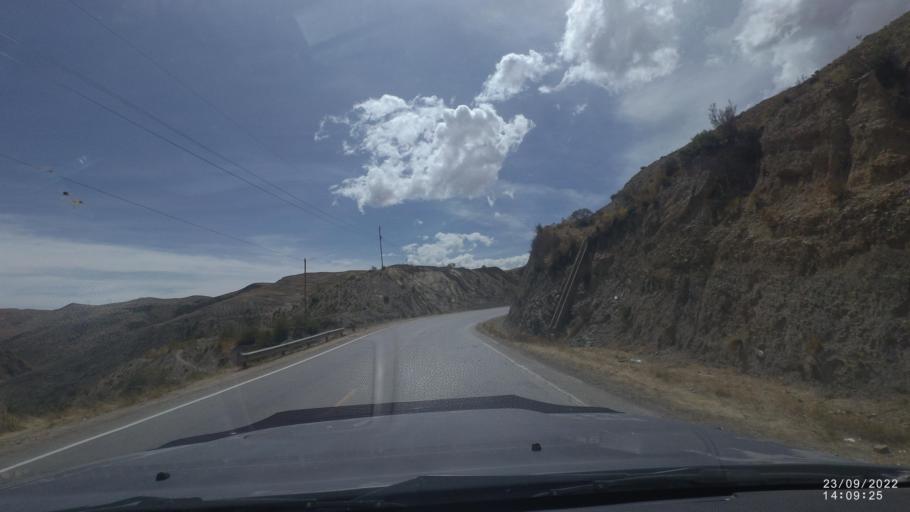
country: BO
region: Cochabamba
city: Sipe Sipe
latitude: -17.7108
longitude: -66.6357
